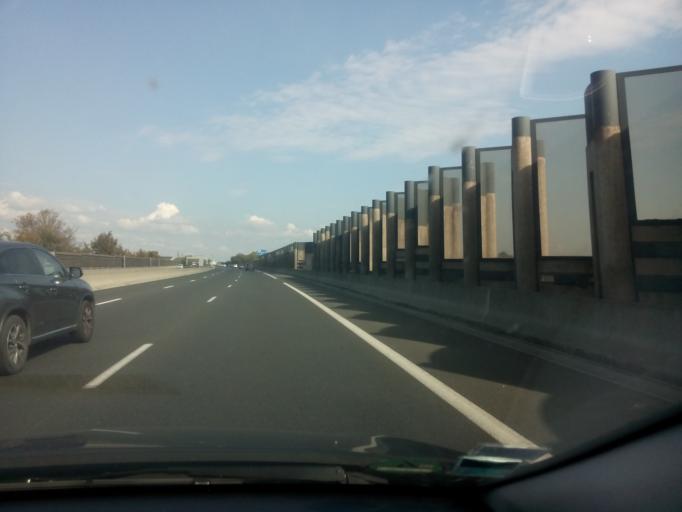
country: FR
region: Pays de la Loire
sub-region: Departement de Maine-et-Loire
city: Angers
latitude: 47.4935
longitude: -0.5269
